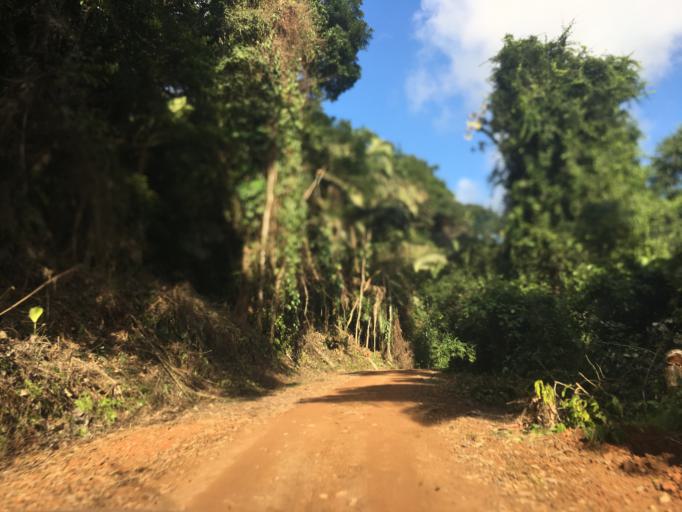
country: BZ
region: Stann Creek
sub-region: Dangriga
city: Dangriga
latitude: 16.7957
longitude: -88.4244
